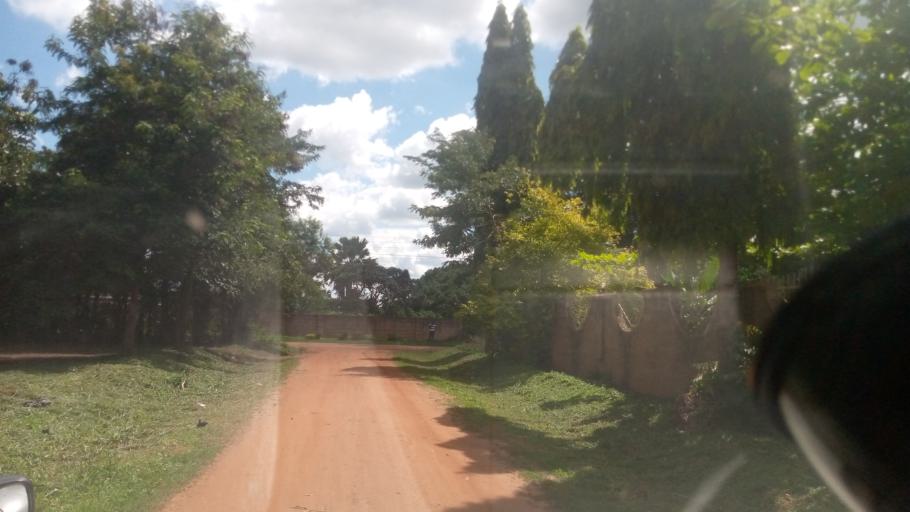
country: UG
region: Northern Region
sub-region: Lira District
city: Lira
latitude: 2.2433
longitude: 32.9035
